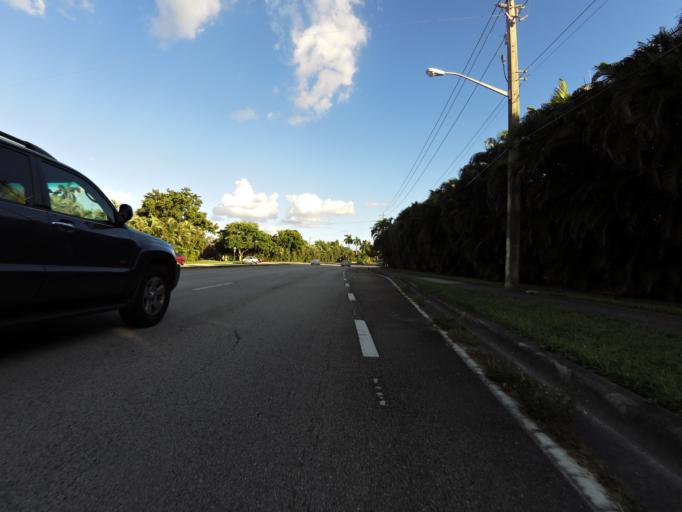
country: US
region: Florida
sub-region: Broward County
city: Cooper City
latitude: 26.0689
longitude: -80.2620
